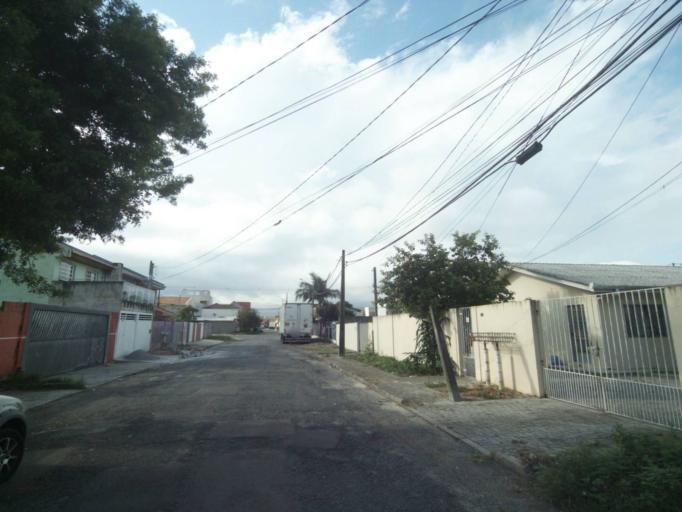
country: BR
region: Parana
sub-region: Pinhais
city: Pinhais
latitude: -25.4581
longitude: -49.2020
